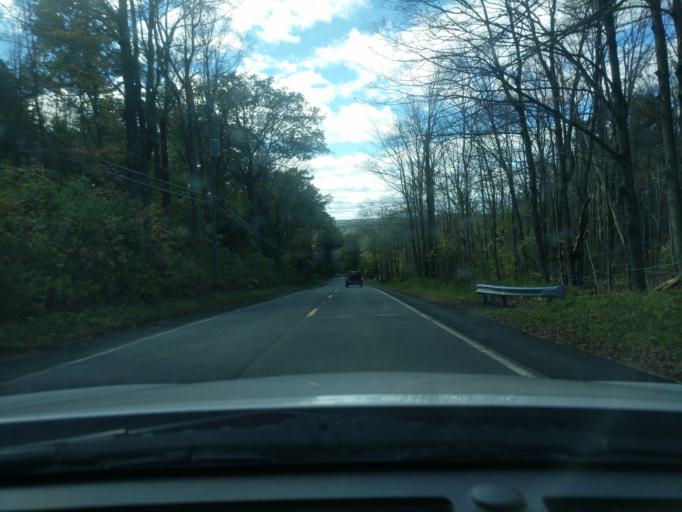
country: US
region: Massachusetts
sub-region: Hampden County
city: Granville
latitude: 42.1796
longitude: -72.9338
